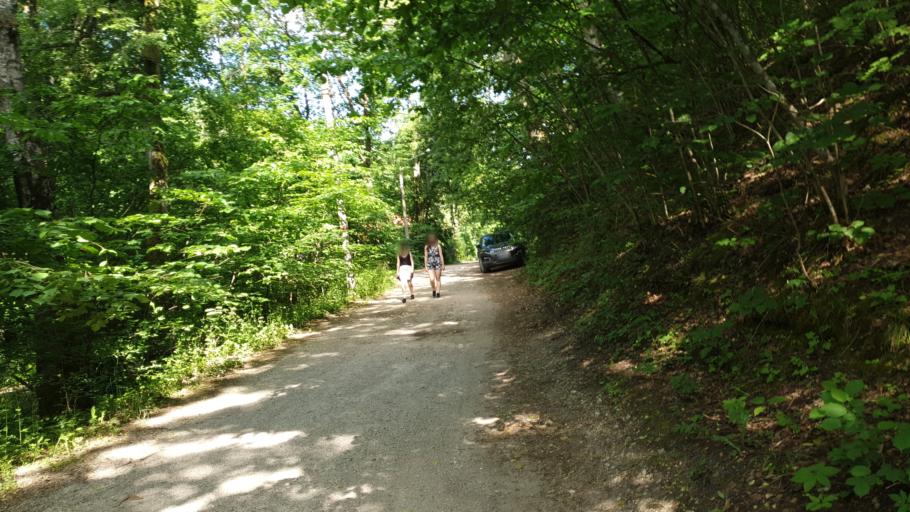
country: LT
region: Vilnius County
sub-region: Vilnius
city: Fabijoniskes
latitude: 54.7846
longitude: 25.3282
